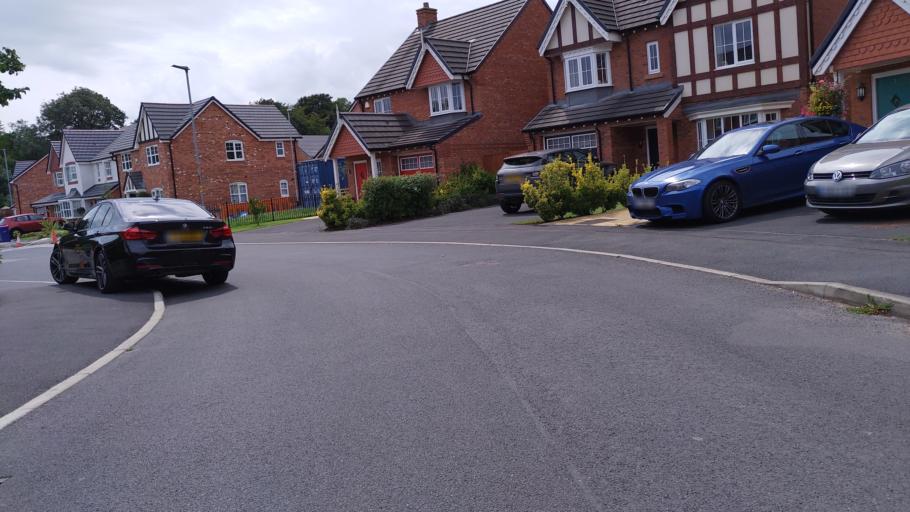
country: GB
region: England
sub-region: Lancashire
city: Chorley
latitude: 53.6383
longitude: -2.6232
